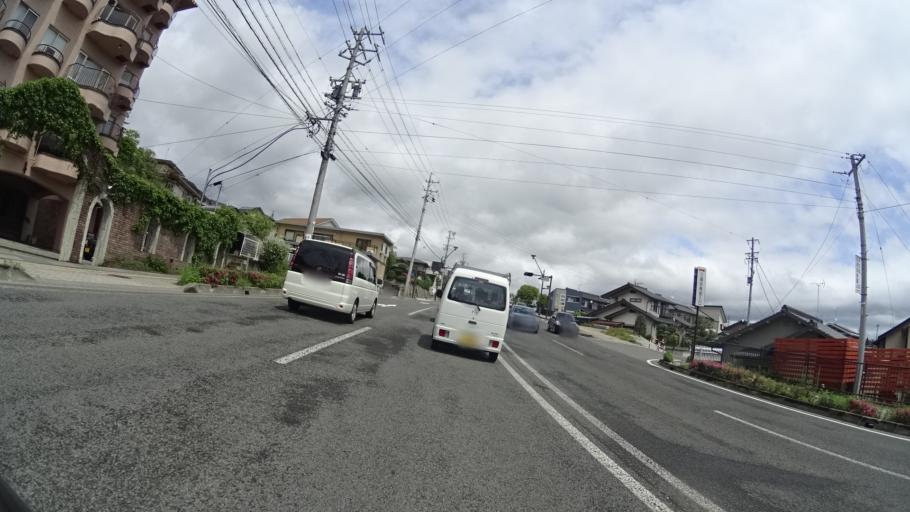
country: JP
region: Nagano
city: Nagano-shi
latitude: 36.6646
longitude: 138.1956
